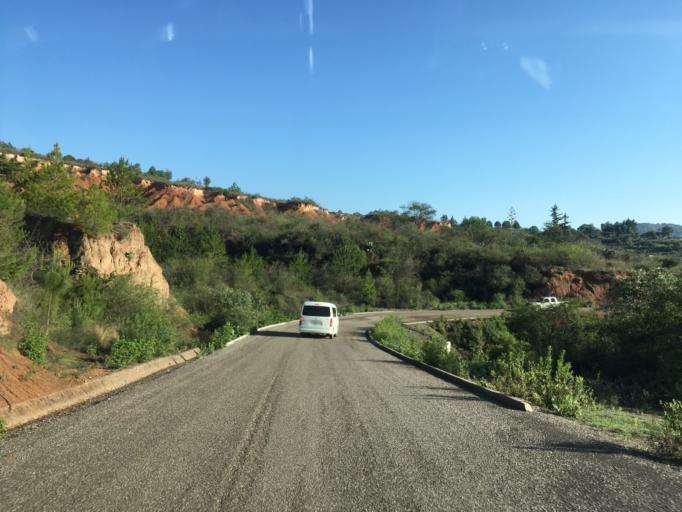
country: MX
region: Oaxaca
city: San Andres Sinaxtla
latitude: 17.5838
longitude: -97.3094
